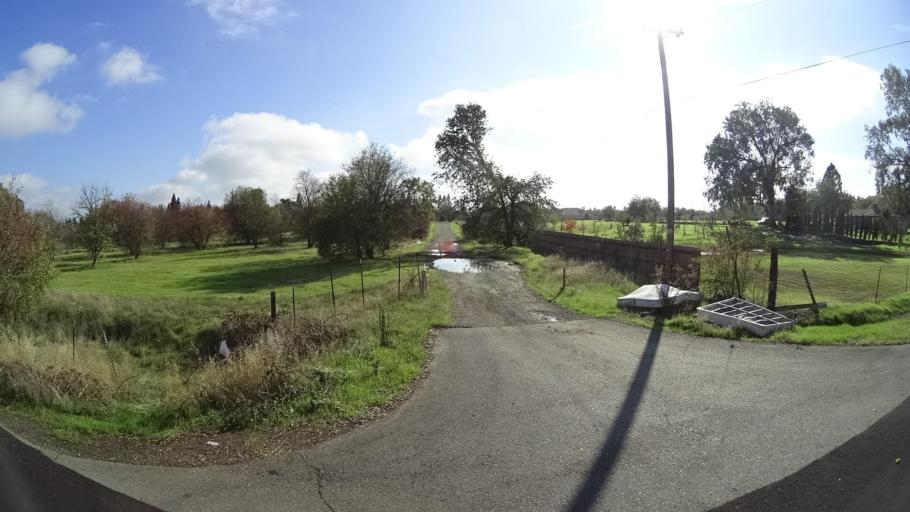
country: US
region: California
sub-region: Sacramento County
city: Elk Grove
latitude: 38.4290
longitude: -121.3692
